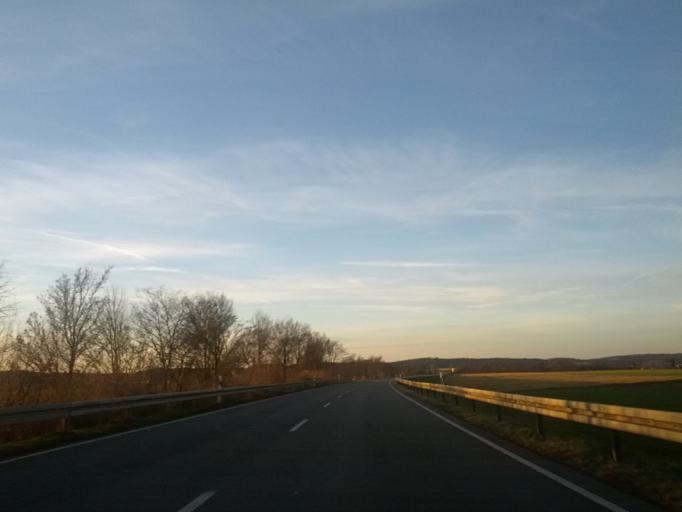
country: DE
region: Baden-Wuerttemberg
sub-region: Tuebingen Region
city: Berkheim
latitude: 48.0386
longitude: 10.1091
